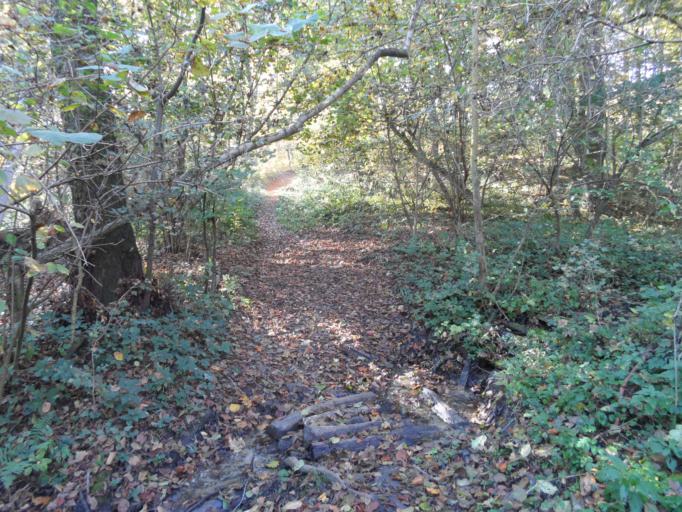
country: HU
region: Veszprem
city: Ajka
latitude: 47.1973
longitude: 17.5788
